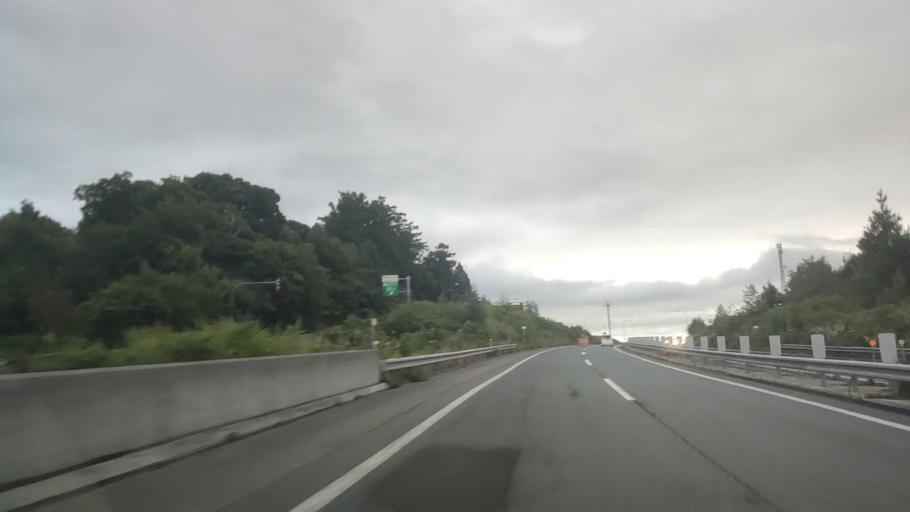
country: JP
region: Hokkaido
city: Nanae
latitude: 41.8972
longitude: 140.7079
